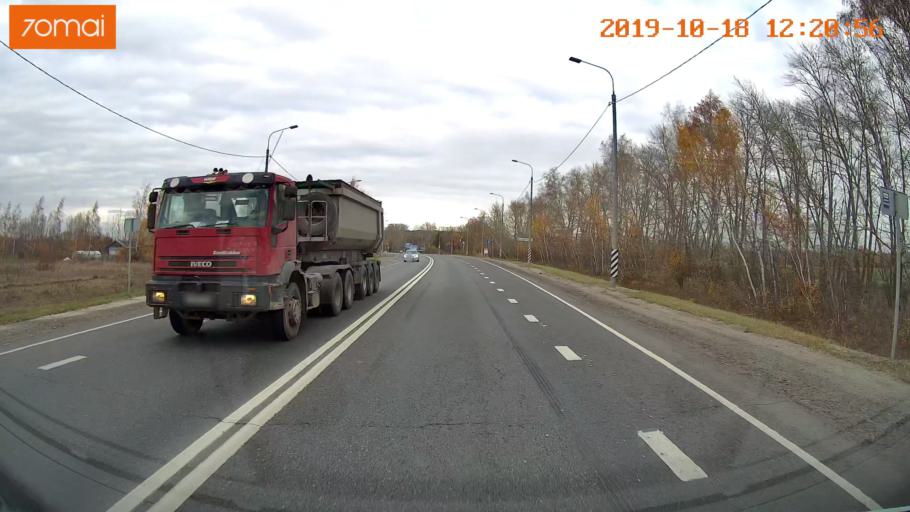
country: RU
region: Rjazan
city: Bagramovo
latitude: 54.5051
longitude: 39.4860
